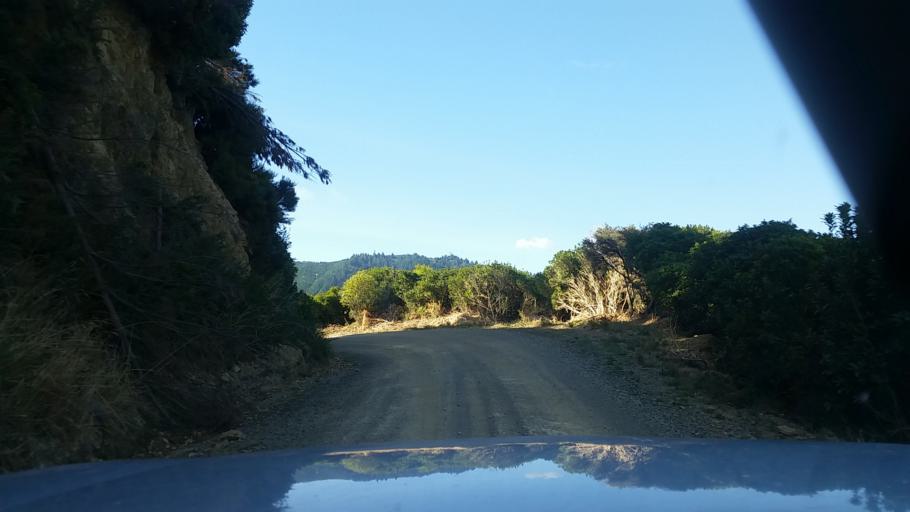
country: NZ
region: Marlborough
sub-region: Marlborough District
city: Picton
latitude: -41.2911
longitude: 174.1676
